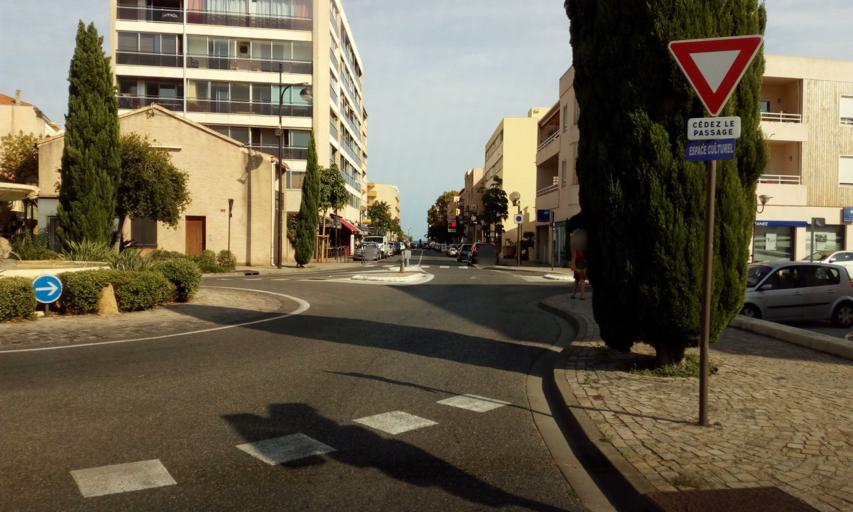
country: FR
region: Provence-Alpes-Cote d'Azur
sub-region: Departement du Var
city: Le Lavandou
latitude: 43.1376
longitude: 6.3629
